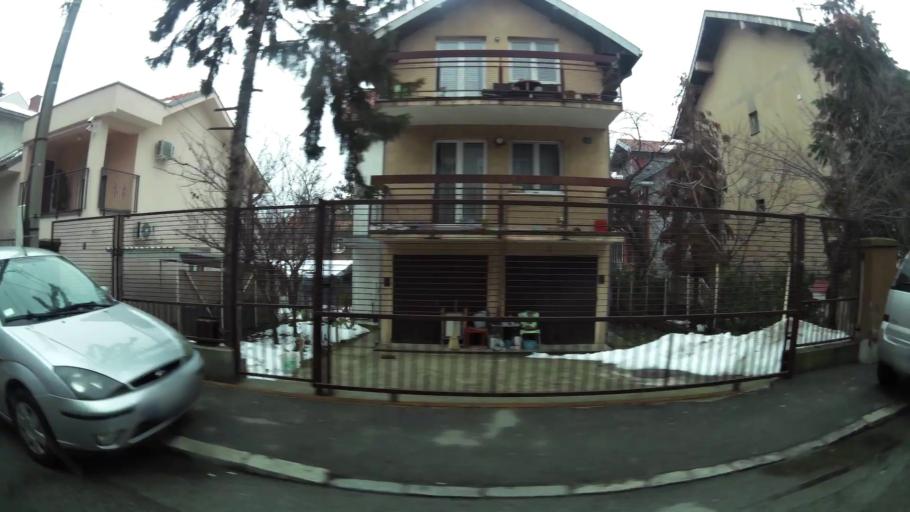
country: RS
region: Central Serbia
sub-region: Belgrade
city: Vozdovac
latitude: 44.7840
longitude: 20.4737
